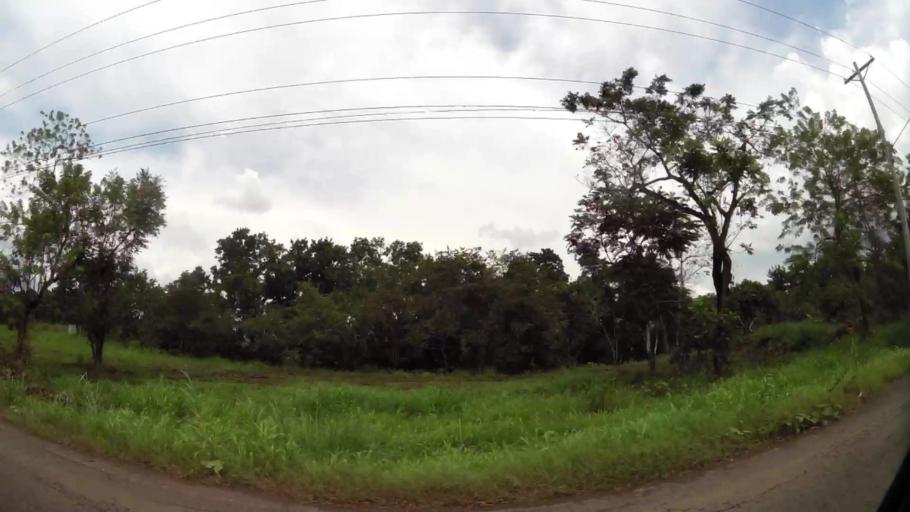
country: PA
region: Panama
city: Cabra Numero Uno
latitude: 9.1125
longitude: -79.3307
